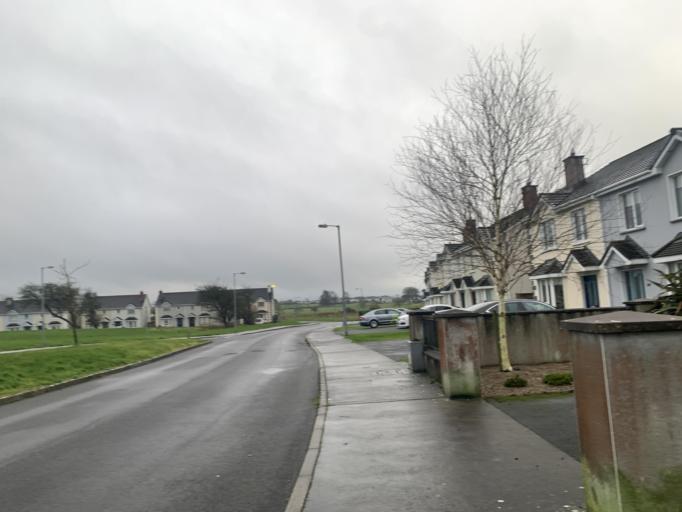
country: IE
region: Connaught
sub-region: County Galway
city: Tuam
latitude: 53.5294
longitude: -8.8557
